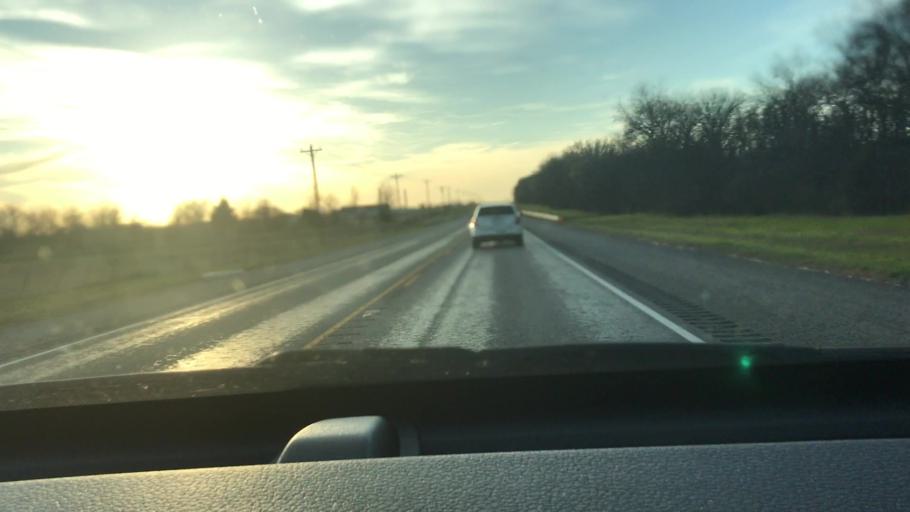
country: US
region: Texas
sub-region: Red River County
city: Clarksville
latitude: 33.6071
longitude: -95.0063
